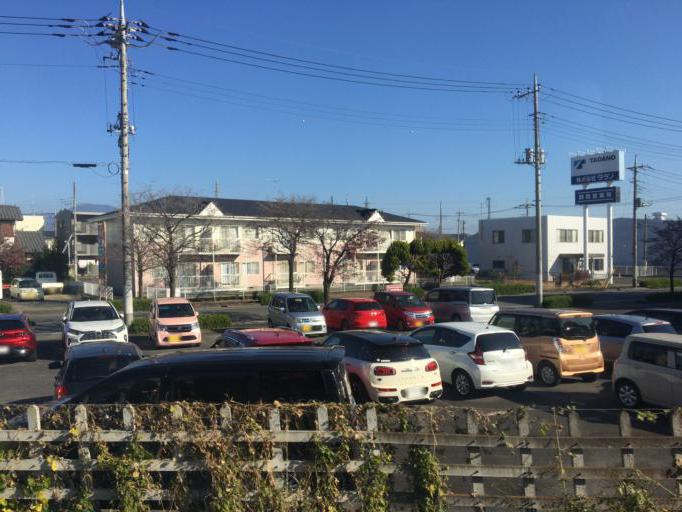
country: JP
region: Gunma
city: Maebashi-shi
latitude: 36.3743
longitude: 139.1033
